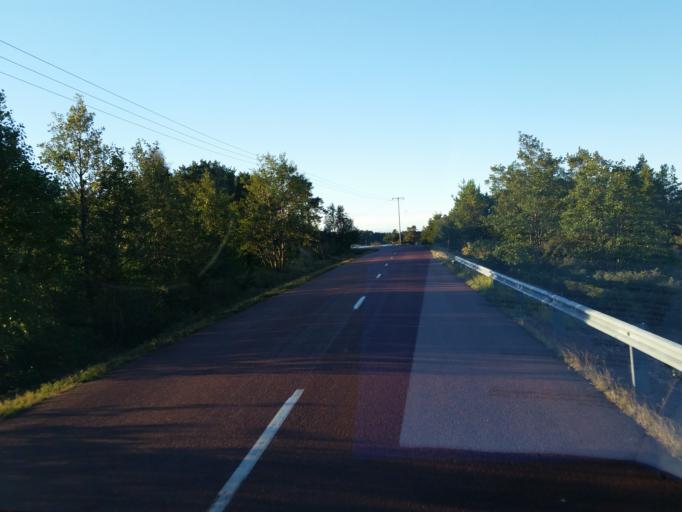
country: AX
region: Alands skaergard
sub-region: Vardoe
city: Vardoe
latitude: 60.3147
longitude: 20.3752
